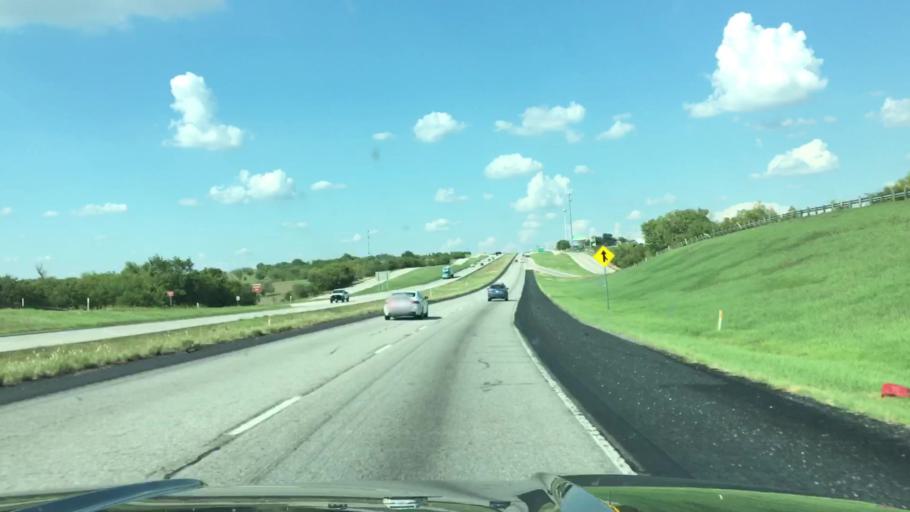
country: US
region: Texas
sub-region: Wise County
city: Rhome
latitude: 33.0563
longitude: -97.4785
